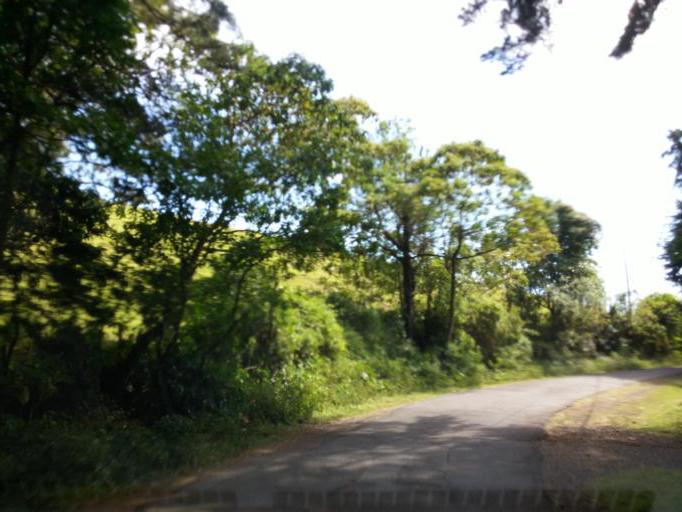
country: CR
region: Heredia
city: Santo Domingo
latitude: 10.0964
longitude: -84.1146
